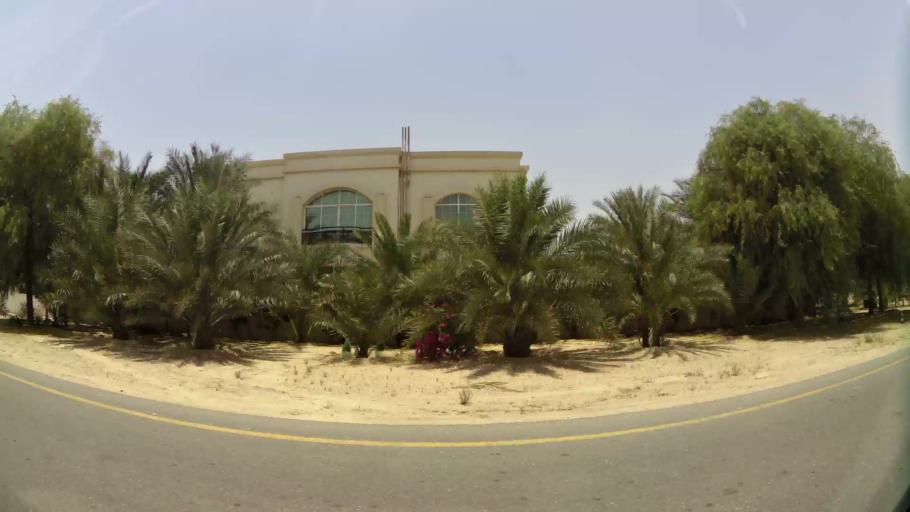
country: AE
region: Ash Shariqah
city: Sharjah
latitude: 25.2514
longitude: 55.4604
